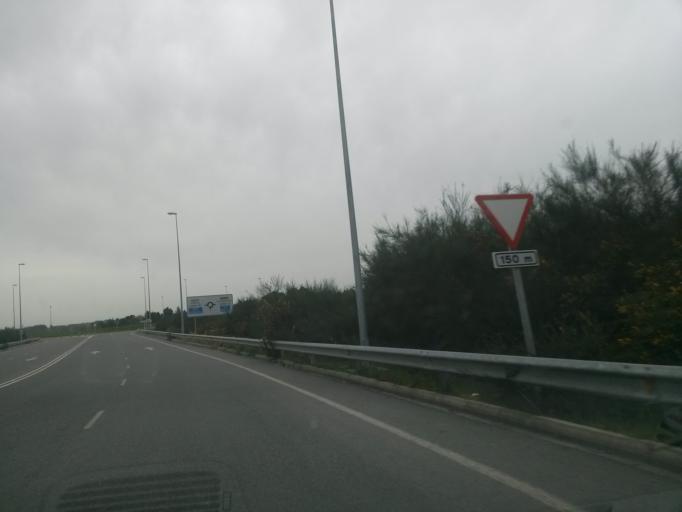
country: ES
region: Galicia
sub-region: Provincia de Lugo
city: Lugo
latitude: 43.0244
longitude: -7.5333
